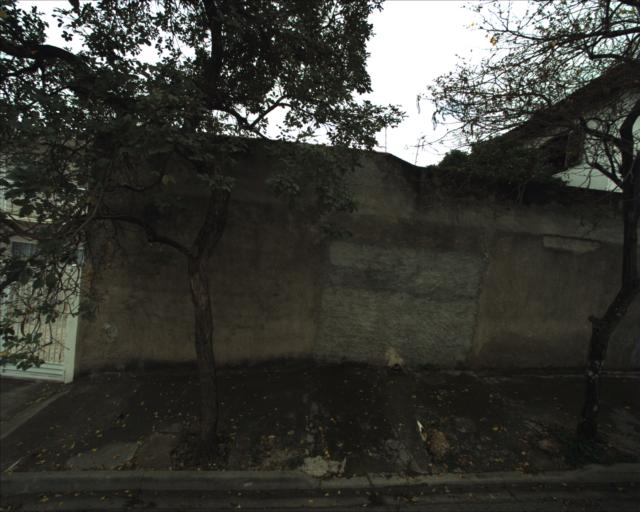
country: BR
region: Sao Paulo
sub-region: Sorocaba
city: Sorocaba
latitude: -23.4992
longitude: -47.4951
